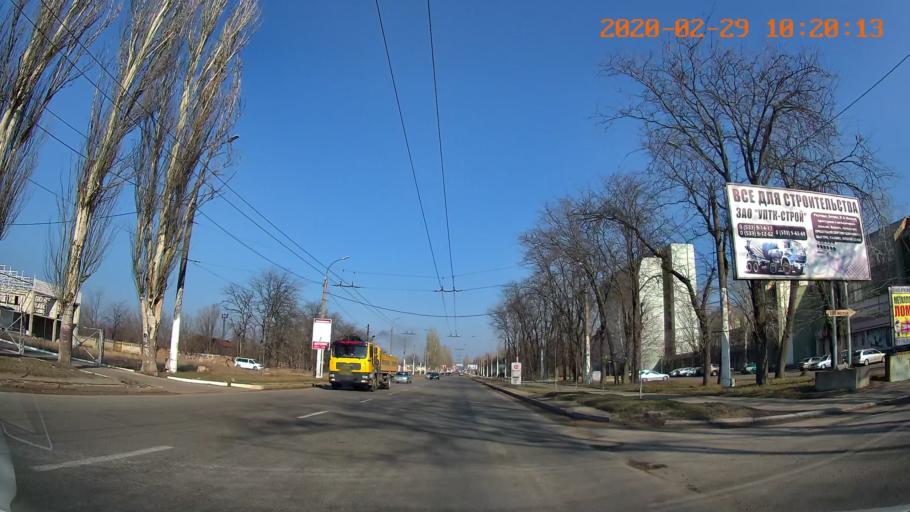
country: MD
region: Telenesti
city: Tiraspolul Nou
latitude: 46.8583
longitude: 29.6110
